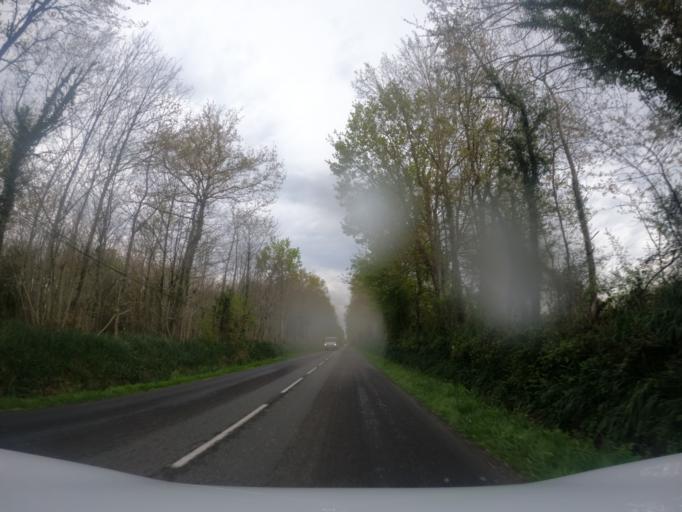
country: FR
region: Pays de la Loire
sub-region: Departement de la Vendee
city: Le Champ-Saint-Pere
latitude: 46.5271
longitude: -1.3625
